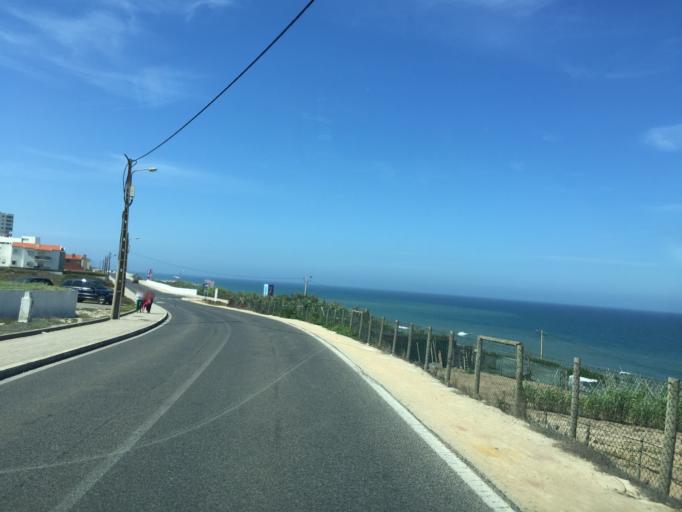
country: PT
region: Lisbon
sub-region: Torres Vedras
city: Silveira
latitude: 39.1439
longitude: -9.3737
